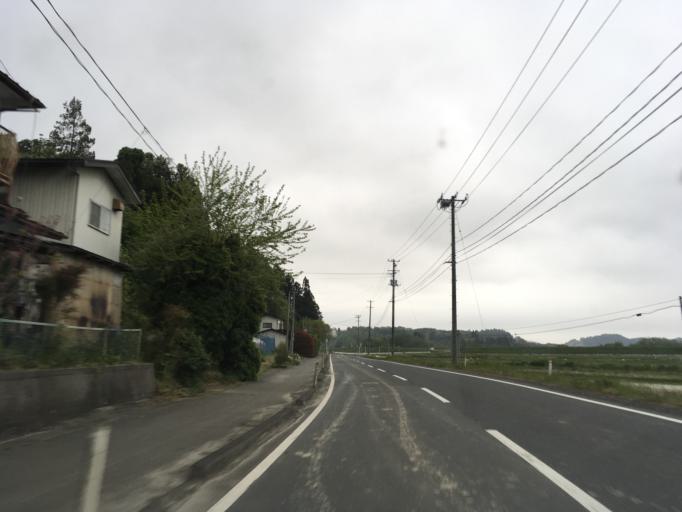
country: JP
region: Miyagi
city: Wakuya
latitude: 38.7230
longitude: 141.2958
